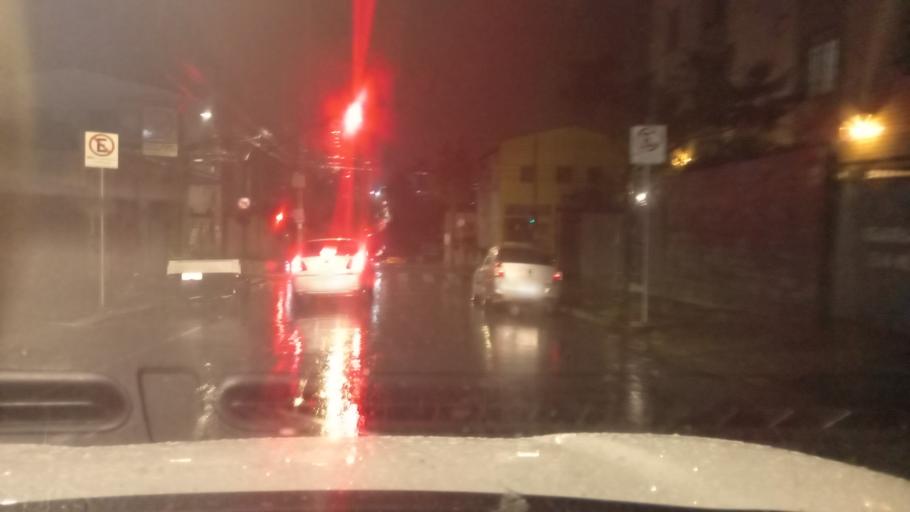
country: BR
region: Minas Gerais
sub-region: Belo Horizonte
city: Belo Horizonte
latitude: -19.9140
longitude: -43.9765
